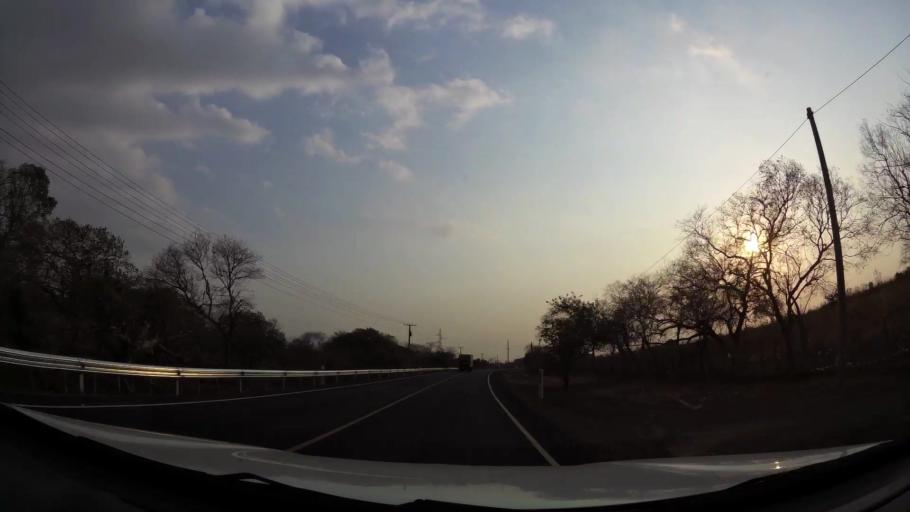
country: NI
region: Leon
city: Nagarote
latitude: 12.2699
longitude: -86.5390
